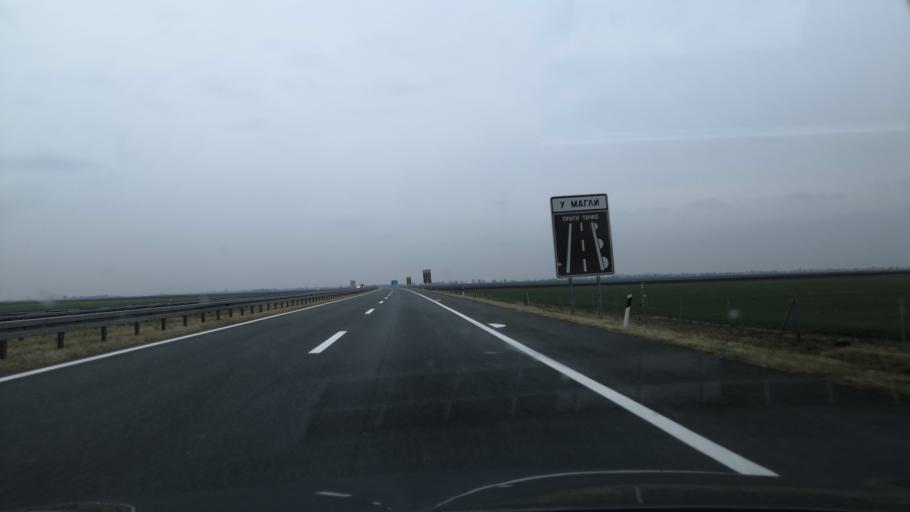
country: RS
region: Autonomna Pokrajina Vojvodina
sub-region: Severnobacki Okrug
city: Backa Topola
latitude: 45.9413
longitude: 19.7111
